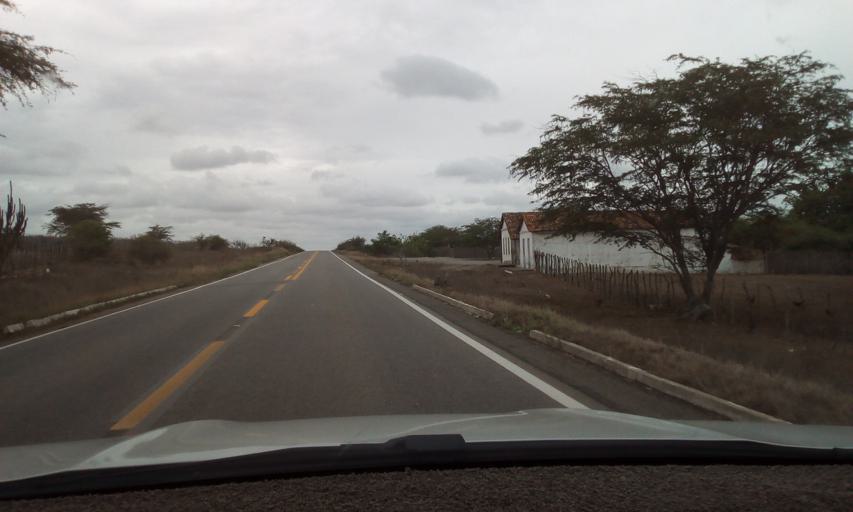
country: BR
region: Paraiba
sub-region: Areia
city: Remigio
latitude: -6.9112
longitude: -35.8634
